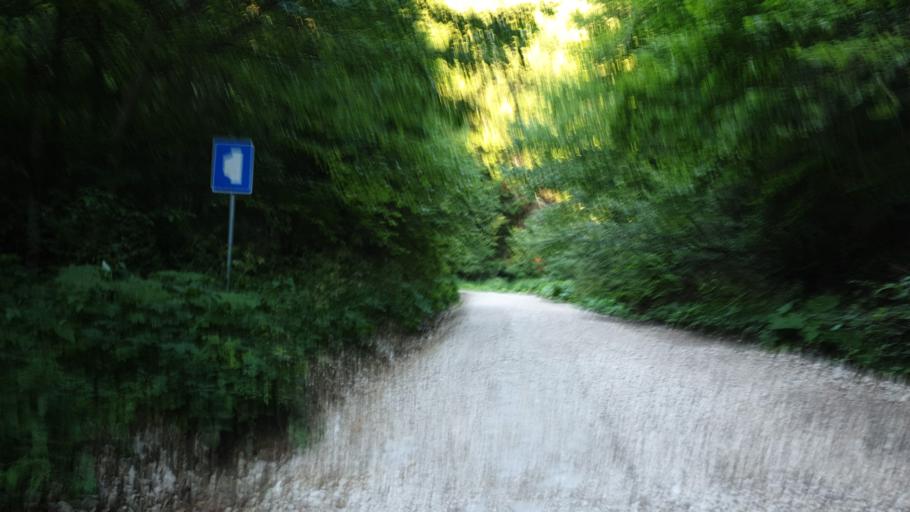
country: RO
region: Brasov
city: Brasov
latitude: 45.6142
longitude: 25.5621
